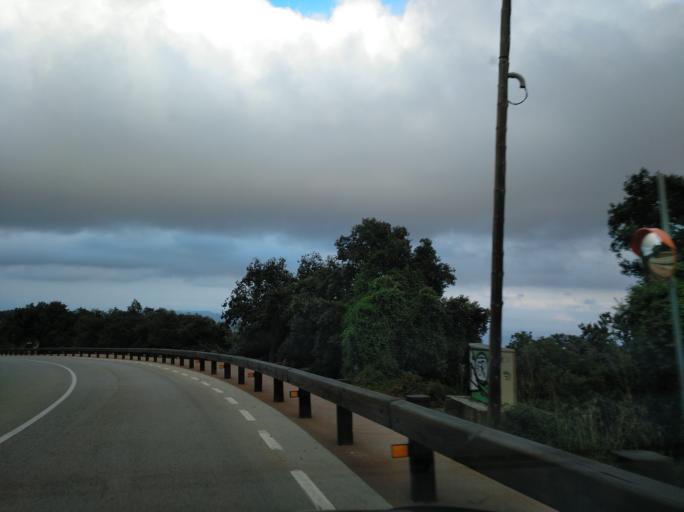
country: ES
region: Catalonia
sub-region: Provincia de Barcelona
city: Sarria-Sant Gervasi
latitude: 41.4247
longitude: 2.1221
